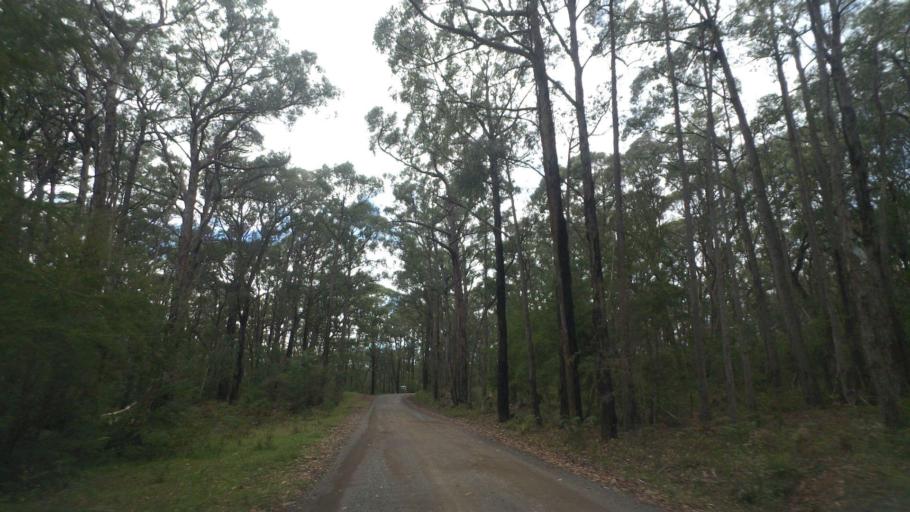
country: AU
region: Victoria
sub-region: Cardinia
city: Gembrook
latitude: -37.8889
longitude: 145.5859
